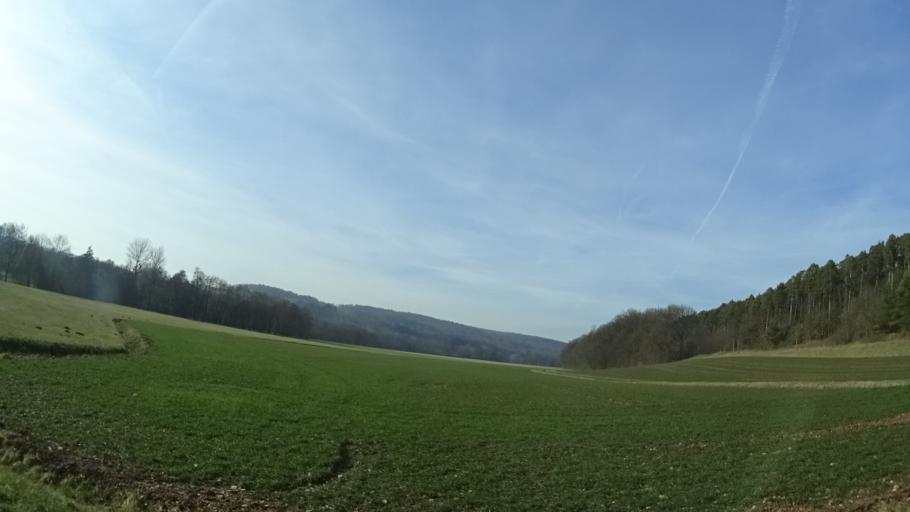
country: DE
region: Bavaria
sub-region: Regierungsbezirk Unterfranken
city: Hohenroth
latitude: 50.3576
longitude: 10.1355
